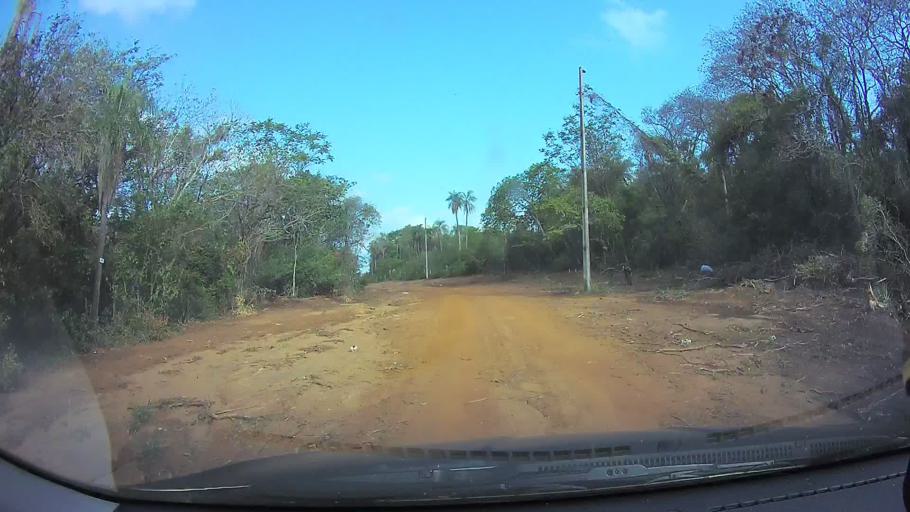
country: PY
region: Cordillera
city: Arroyos y Esteros
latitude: -25.0145
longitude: -57.1978
